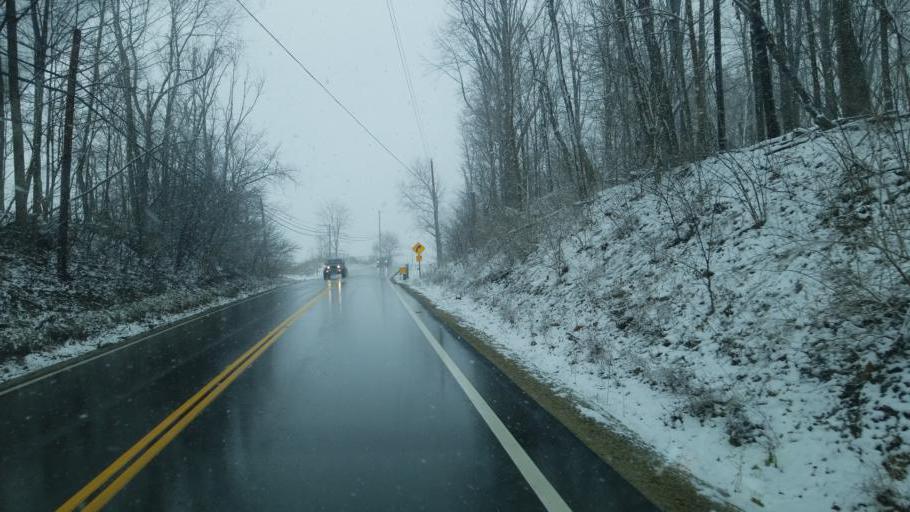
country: US
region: Ohio
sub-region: Preble County
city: New Paris
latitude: 39.8408
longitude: -84.7925
